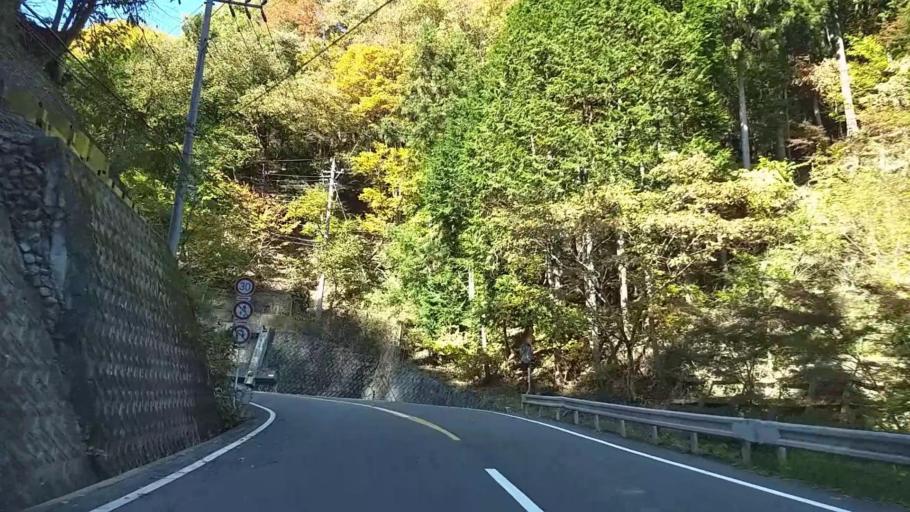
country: JP
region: Yamanashi
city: Otsuki
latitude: 35.7276
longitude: 138.9869
